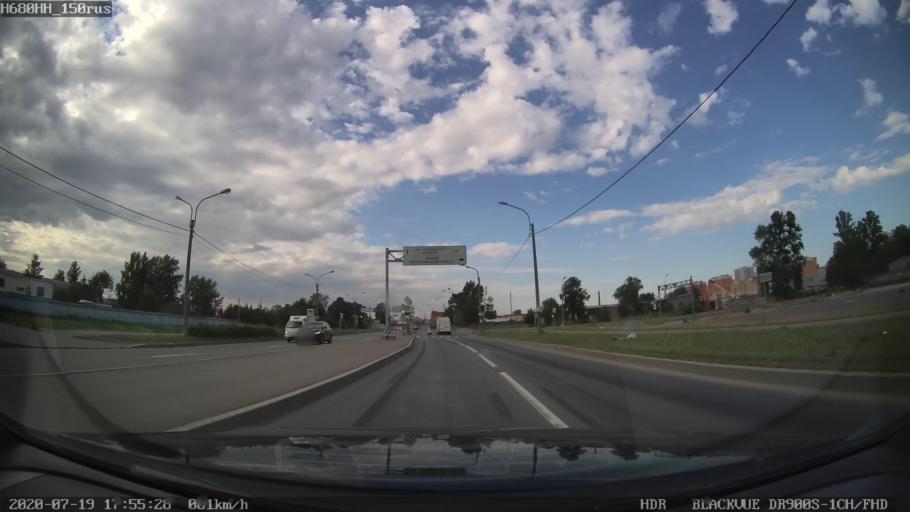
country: RU
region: St.-Petersburg
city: Admiralteisky
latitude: 59.8954
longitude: 30.3008
